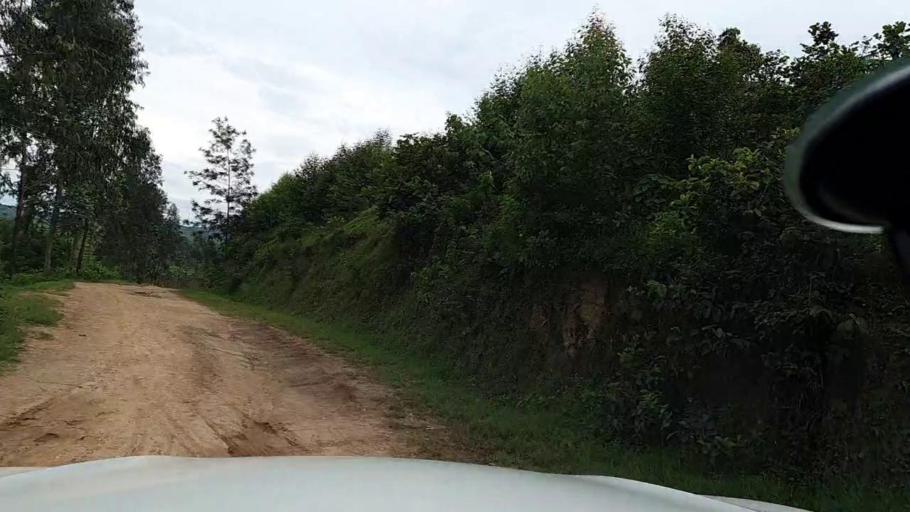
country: RW
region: Southern Province
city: Gitarama
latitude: -2.0915
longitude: 29.6406
